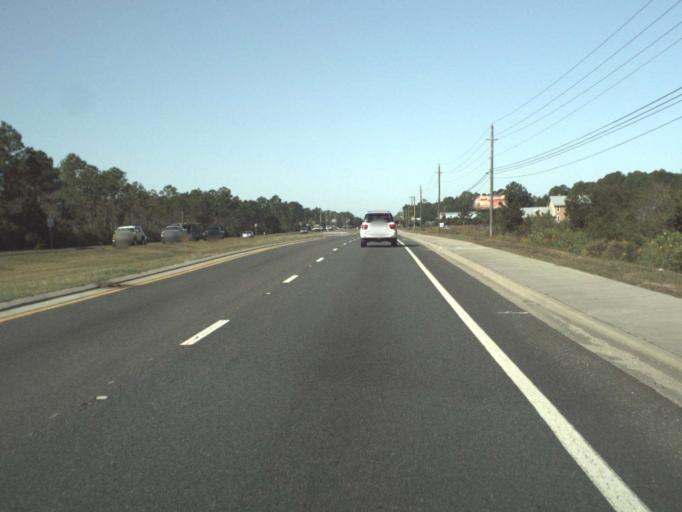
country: US
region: Florida
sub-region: Walton County
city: Seaside
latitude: 30.3740
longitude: -86.2220
